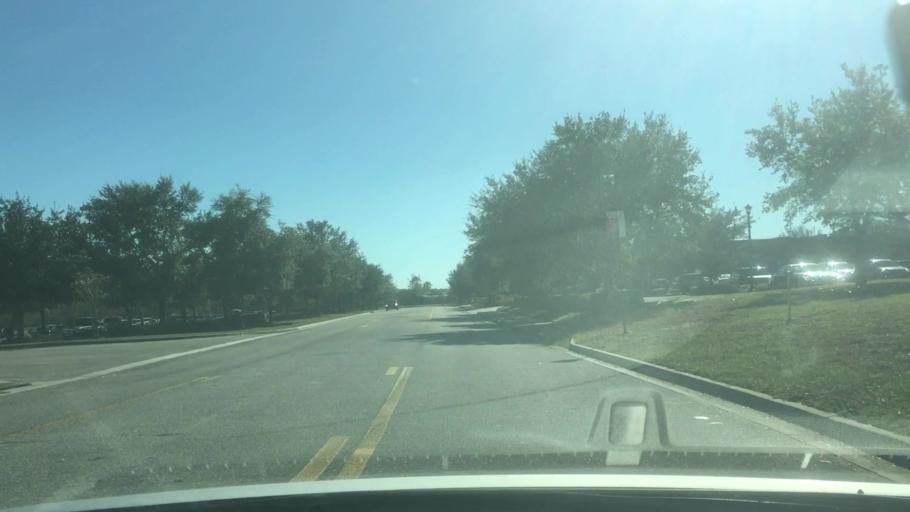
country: US
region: Florida
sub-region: Duval County
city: Jacksonville
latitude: 30.3329
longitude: -81.5512
